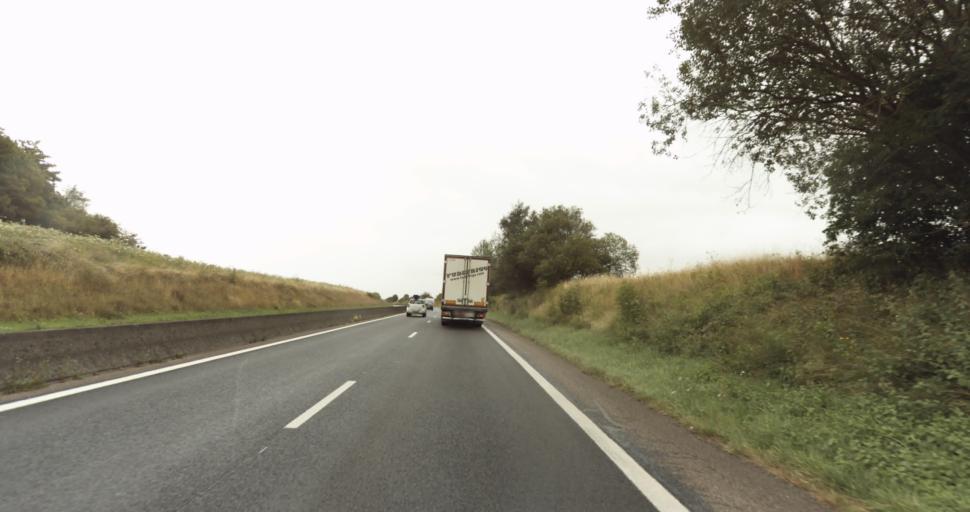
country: FR
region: Haute-Normandie
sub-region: Departement de l'Eure
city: Normanville
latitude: 49.0760
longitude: 1.1863
